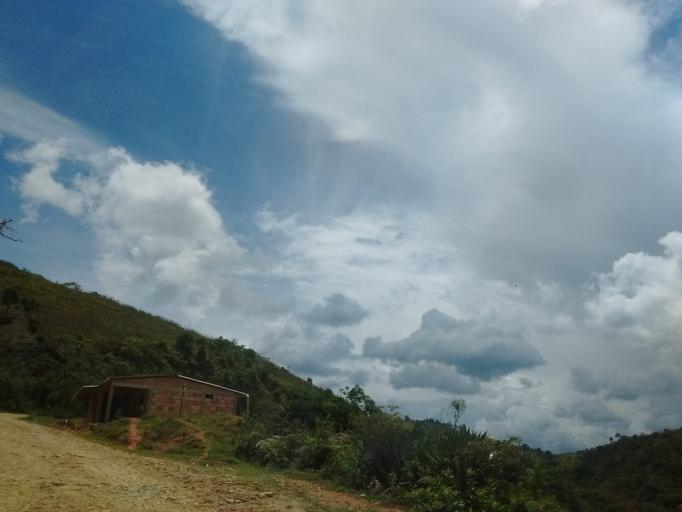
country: CO
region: Cauca
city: Villa Rica
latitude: 2.5979
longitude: -76.7583
